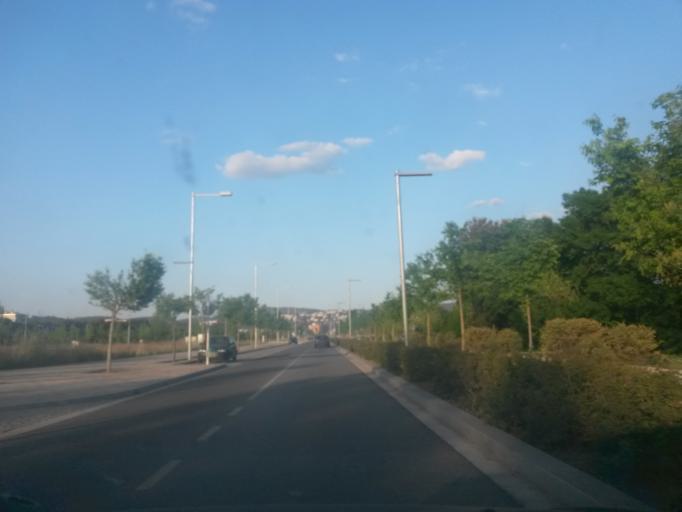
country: ES
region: Catalonia
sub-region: Provincia de Girona
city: Salt
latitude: 41.9895
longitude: 2.7970
